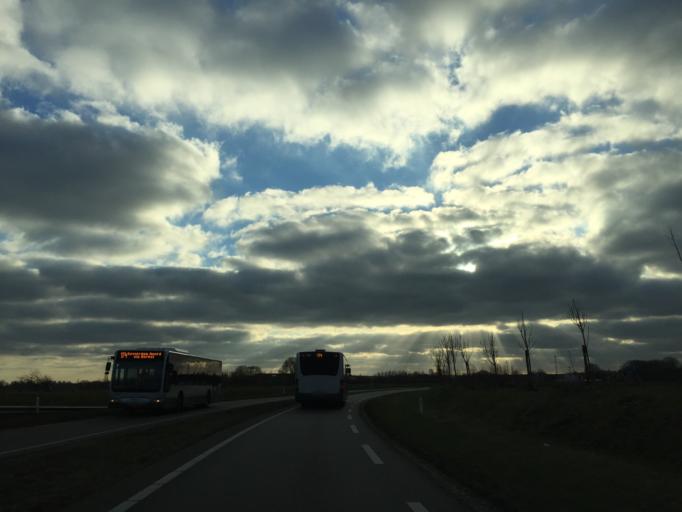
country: NL
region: South Holland
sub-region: Gemeente Pijnacker-Nootdorp
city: Pijnacker
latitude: 52.0018
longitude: 4.4079
